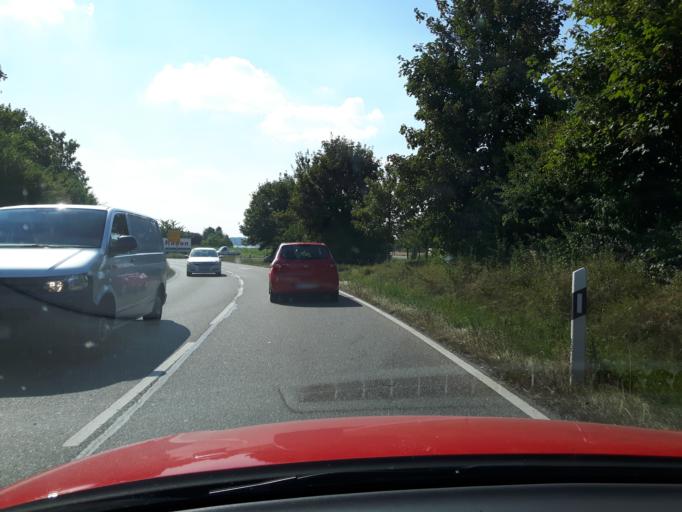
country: DE
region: Baden-Wuerttemberg
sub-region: Regierungsbezirk Stuttgart
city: Nordheim
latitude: 49.1139
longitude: 9.1309
